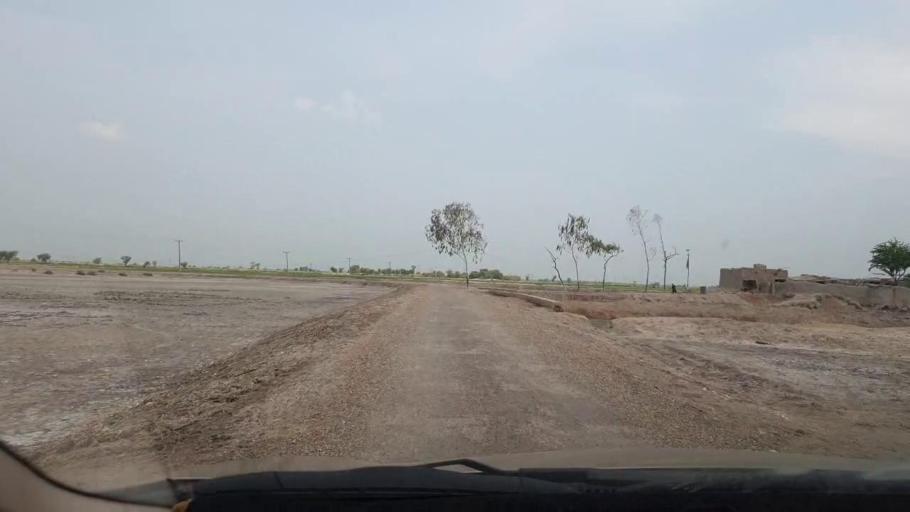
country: PK
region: Sindh
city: Larkana
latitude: 27.5179
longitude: 68.1255
